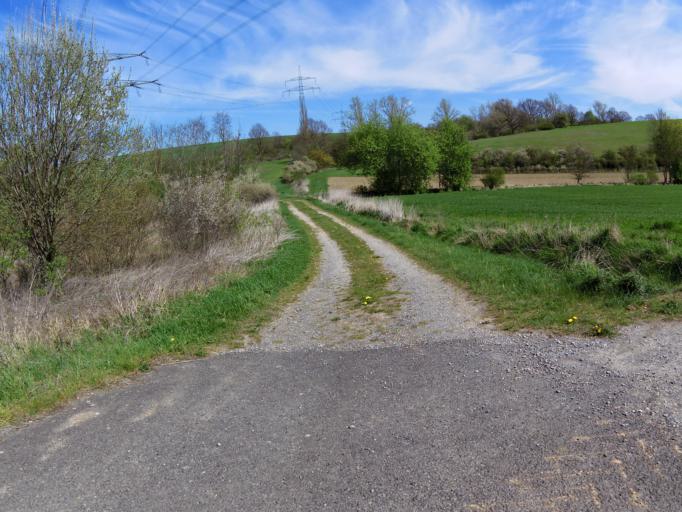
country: DE
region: Bavaria
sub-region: Regierungsbezirk Unterfranken
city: Rottendorf
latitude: 49.7826
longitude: 10.0478
